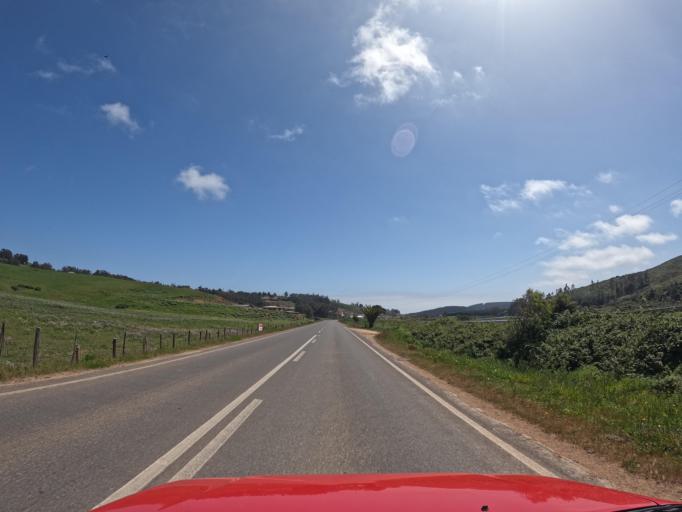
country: CL
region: O'Higgins
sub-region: Provincia de Colchagua
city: Santa Cruz
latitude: -34.6505
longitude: -72.0274
